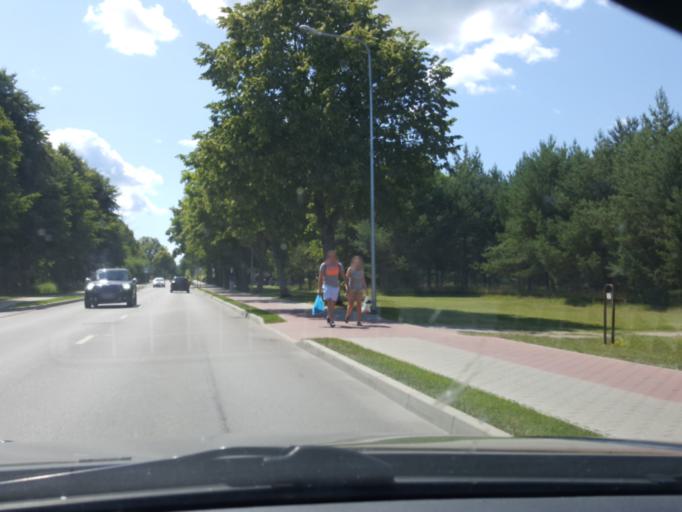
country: LT
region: Klaipedos apskritis
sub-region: Klaipeda
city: Palanga
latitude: 55.9341
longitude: 21.0767
